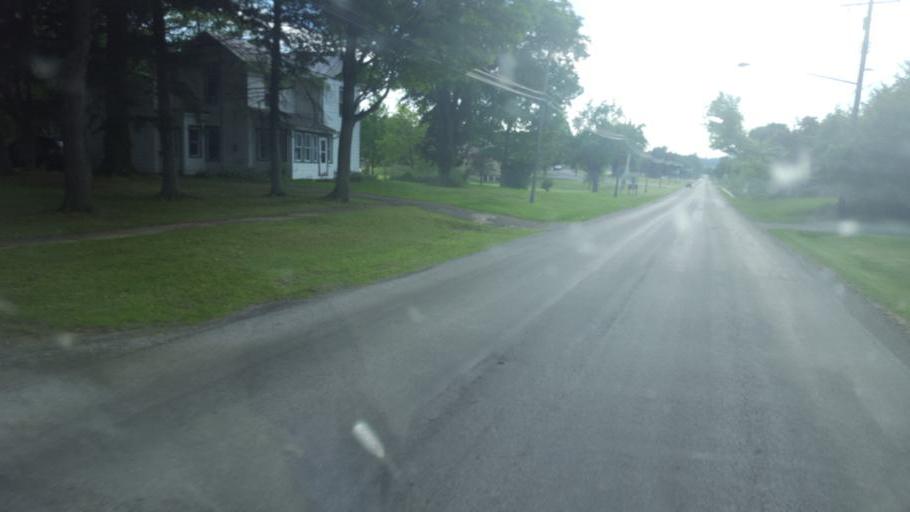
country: US
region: Ohio
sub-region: Ashland County
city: Ashland
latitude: 40.7731
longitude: -82.2678
